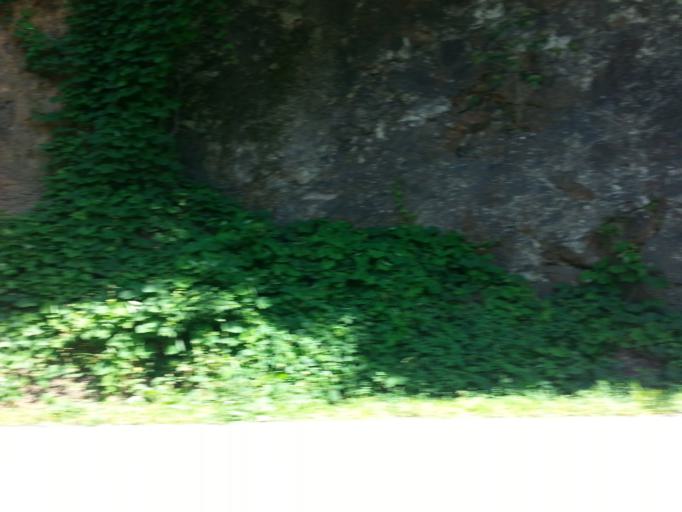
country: US
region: Virginia
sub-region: Lee County
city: Pennington Gap
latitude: 36.7780
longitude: -83.0409
